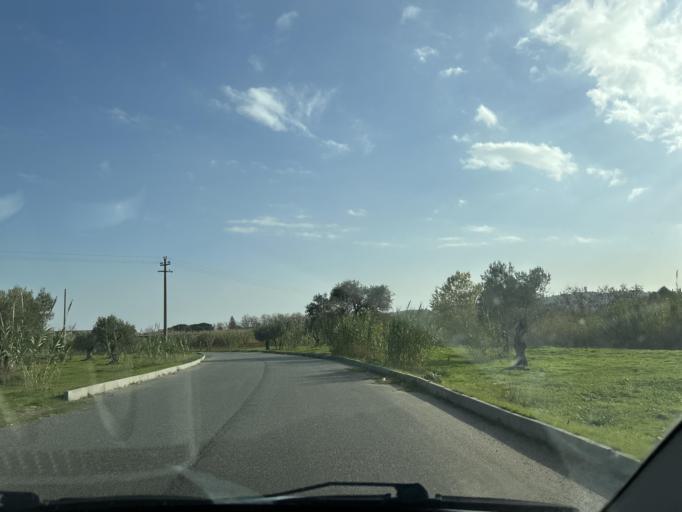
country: IT
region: Calabria
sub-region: Provincia di Catanzaro
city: Montepaone Lido
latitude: 38.7139
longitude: 16.5297
